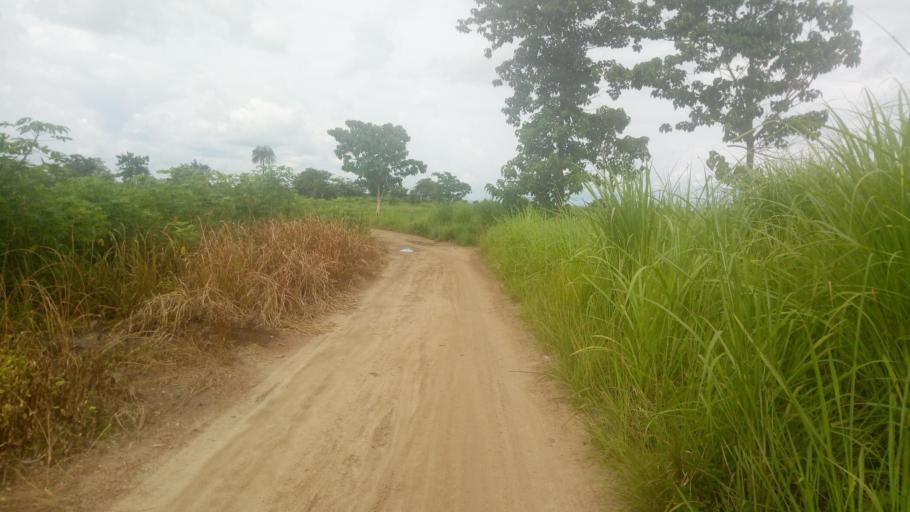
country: SL
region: Northern Province
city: Magburaka
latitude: 8.6710
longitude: -12.0283
